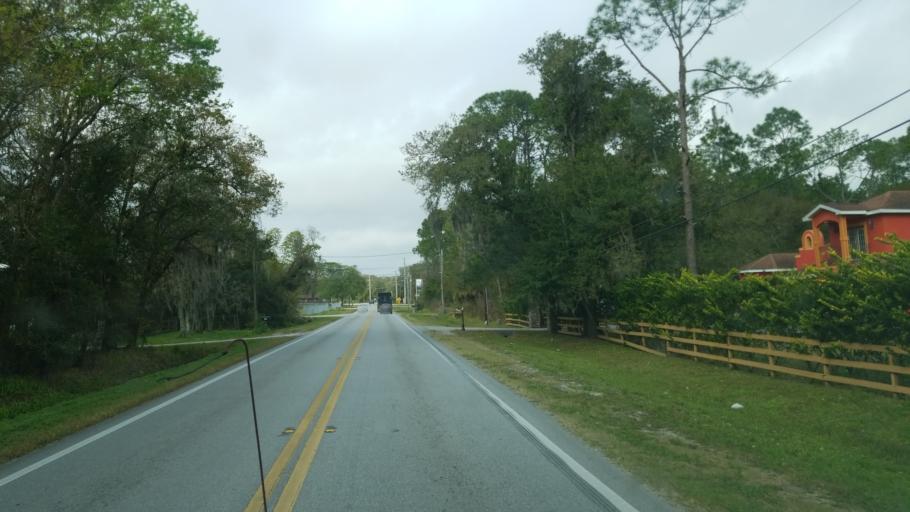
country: US
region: Florida
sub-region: Polk County
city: Winston
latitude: 28.0585
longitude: -82.0121
